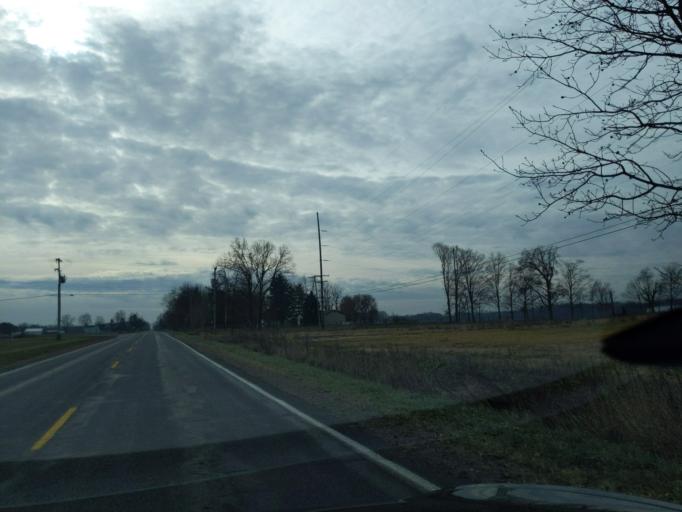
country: US
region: Michigan
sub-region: Ingham County
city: Holt
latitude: 42.6123
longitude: -84.5231
